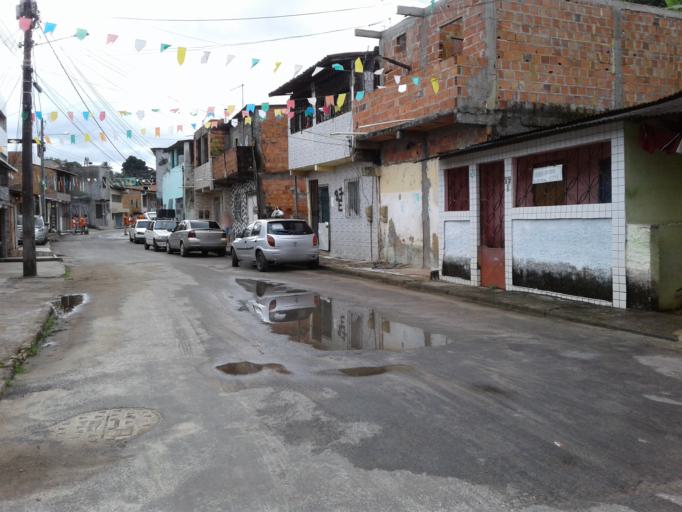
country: BR
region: Bahia
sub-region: Salvador
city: Salvador
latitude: -12.8827
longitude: -38.4738
